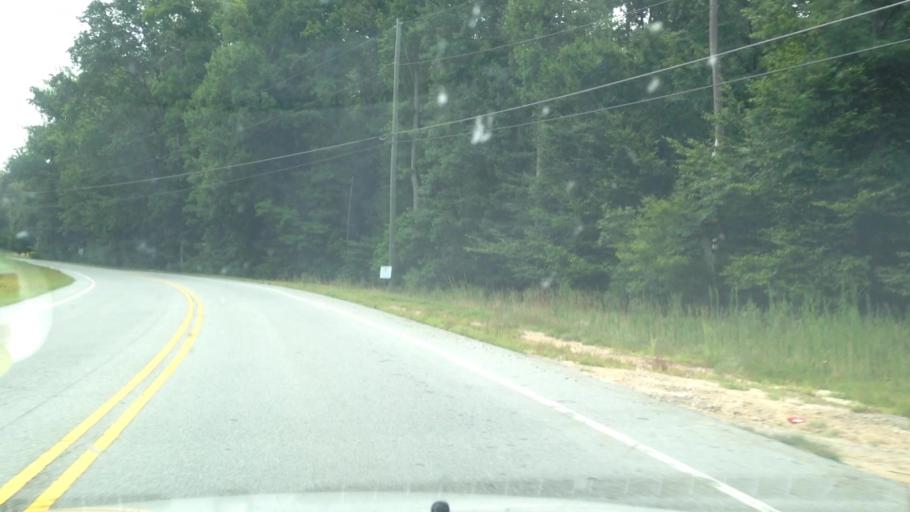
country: US
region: North Carolina
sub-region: Rockingham County
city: Wentworth
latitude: 36.3968
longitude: -79.7884
